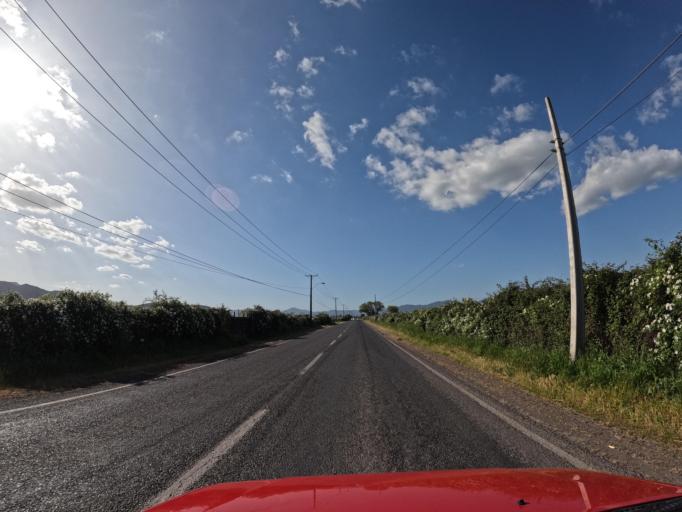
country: CL
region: Maule
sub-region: Provincia de Curico
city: Rauco
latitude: -34.9234
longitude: -71.2769
